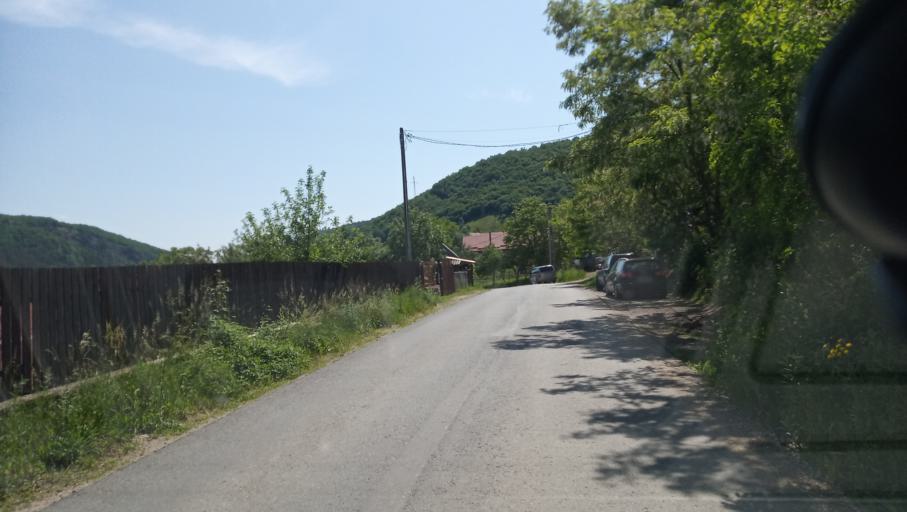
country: RO
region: Cluj
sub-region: Comuna Gilau
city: Gilau
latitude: 46.7311
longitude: 23.3276
